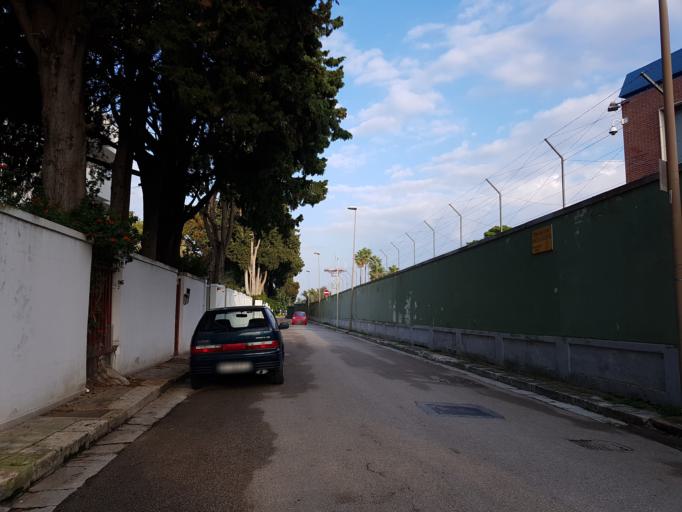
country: IT
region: Apulia
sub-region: Provincia di Brindisi
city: Materdomini
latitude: 40.6485
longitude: 17.9477
